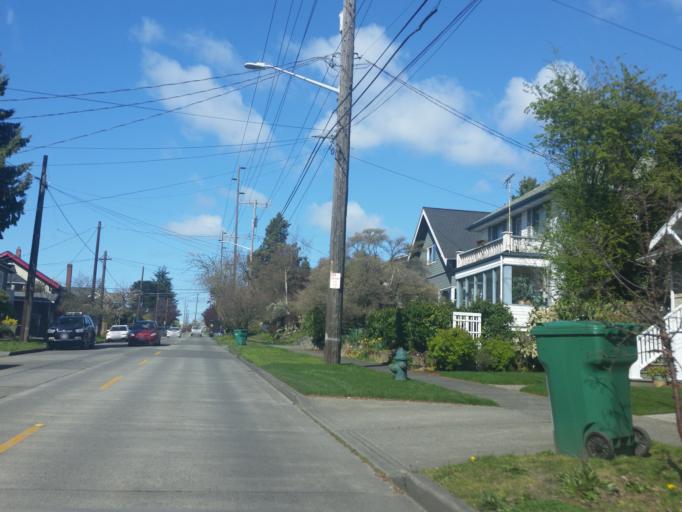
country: US
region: Washington
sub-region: King County
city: Seattle
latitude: 47.6786
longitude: -122.3605
